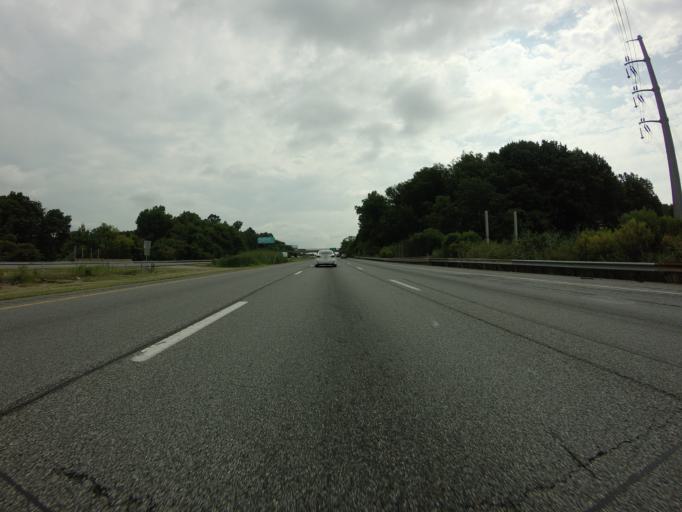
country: US
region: Pennsylvania
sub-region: Delaware County
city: Trainer
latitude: 39.8357
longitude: -75.4195
